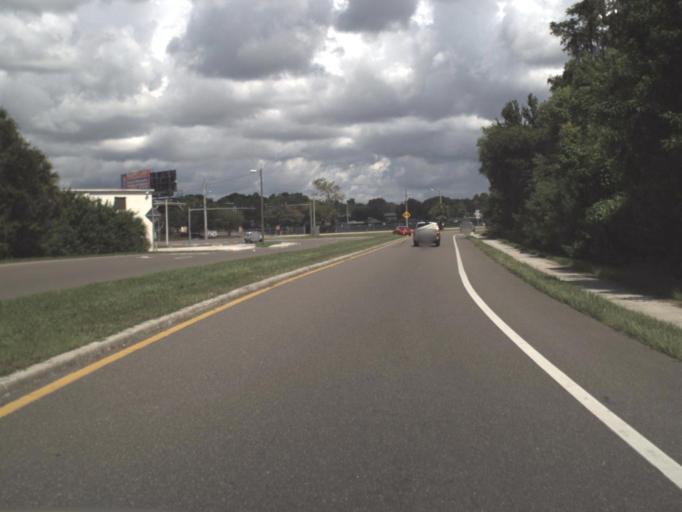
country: US
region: Florida
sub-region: Hillsborough County
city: East Lake-Orient Park
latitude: 27.9731
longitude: -82.4124
